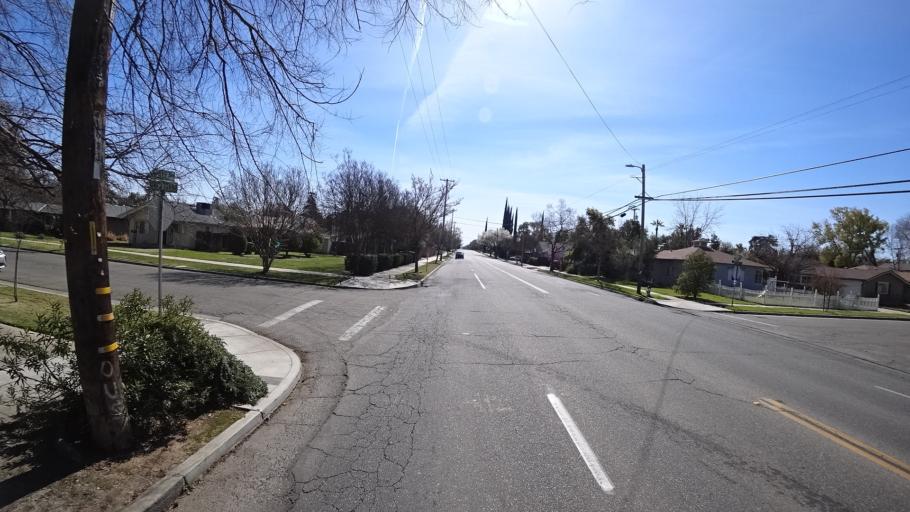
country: US
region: California
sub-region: Fresno County
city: Fresno
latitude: 36.7776
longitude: -119.8086
